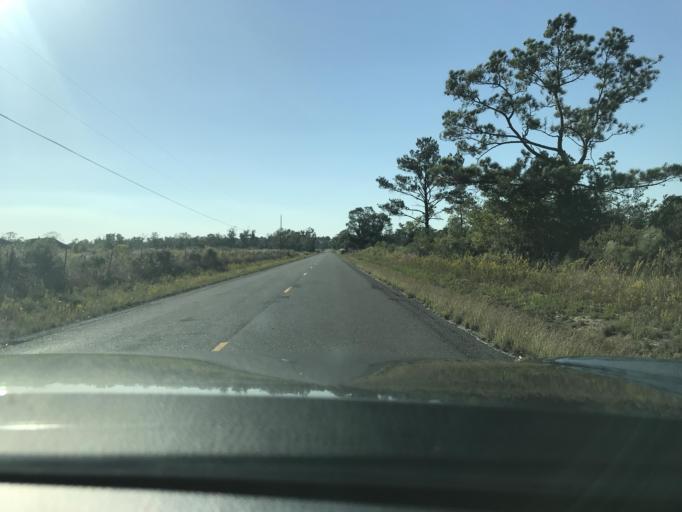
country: US
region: Louisiana
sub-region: Calcasieu Parish
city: Moss Bluff
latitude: 30.3153
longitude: -93.2608
